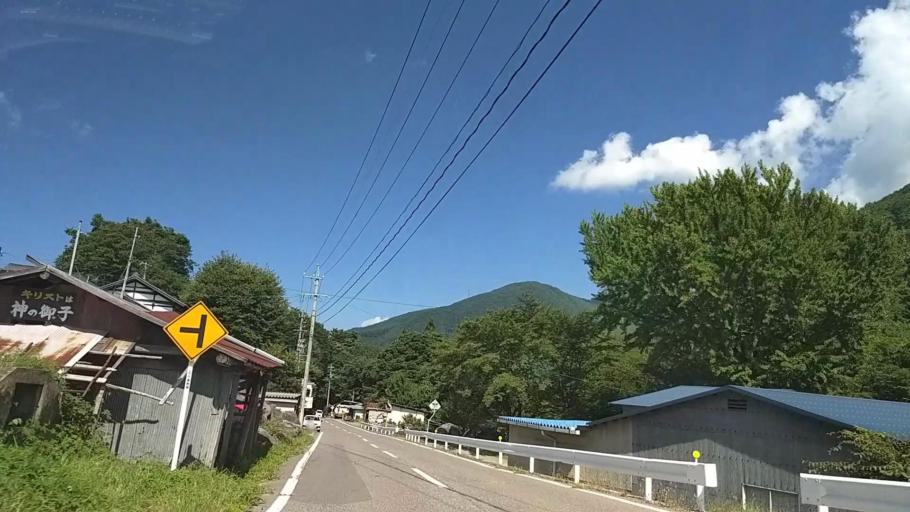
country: JP
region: Nagano
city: Matsumoto
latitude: 36.2083
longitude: 138.0569
